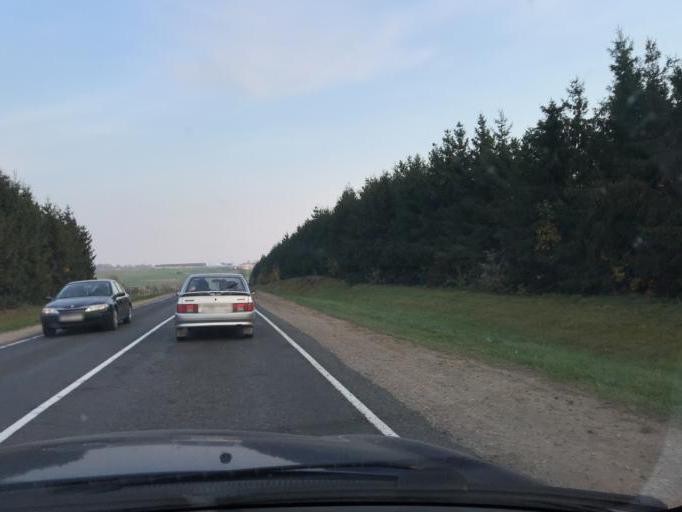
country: BY
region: Grodnenskaya
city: Karelichy
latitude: 53.5903
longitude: 26.0935
